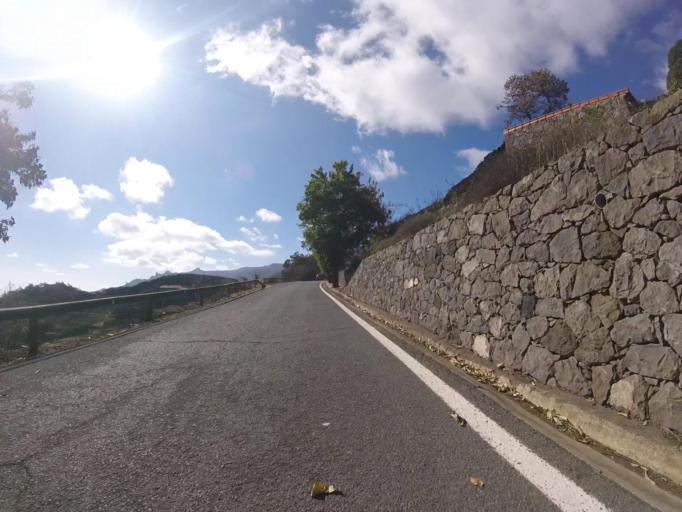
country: ES
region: Canary Islands
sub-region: Provincia de Las Palmas
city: Valleseco
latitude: 28.0149
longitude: -15.5836
